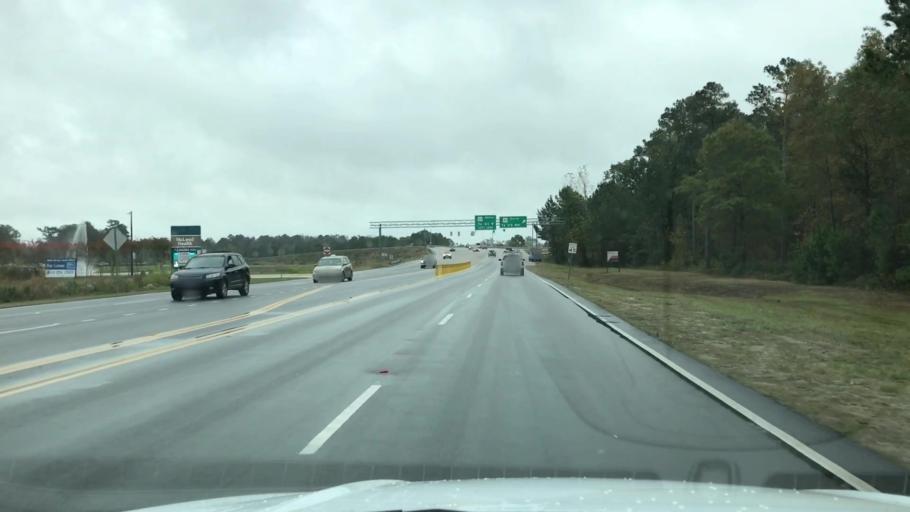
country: US
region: South Carolina
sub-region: Horry County
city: Myrtle Beach
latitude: 33.7580
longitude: -78.8568
